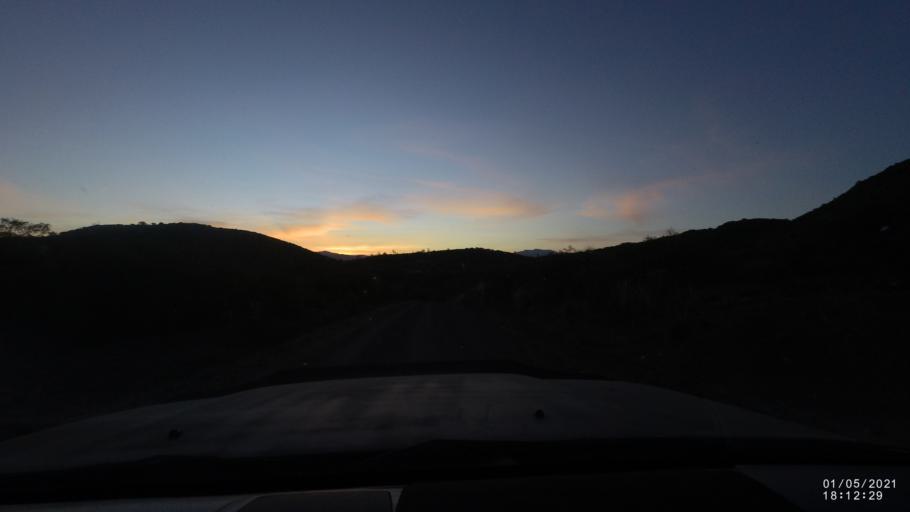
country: BO
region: Cochabamba
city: Capinota
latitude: -17.6780
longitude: -66.2016
